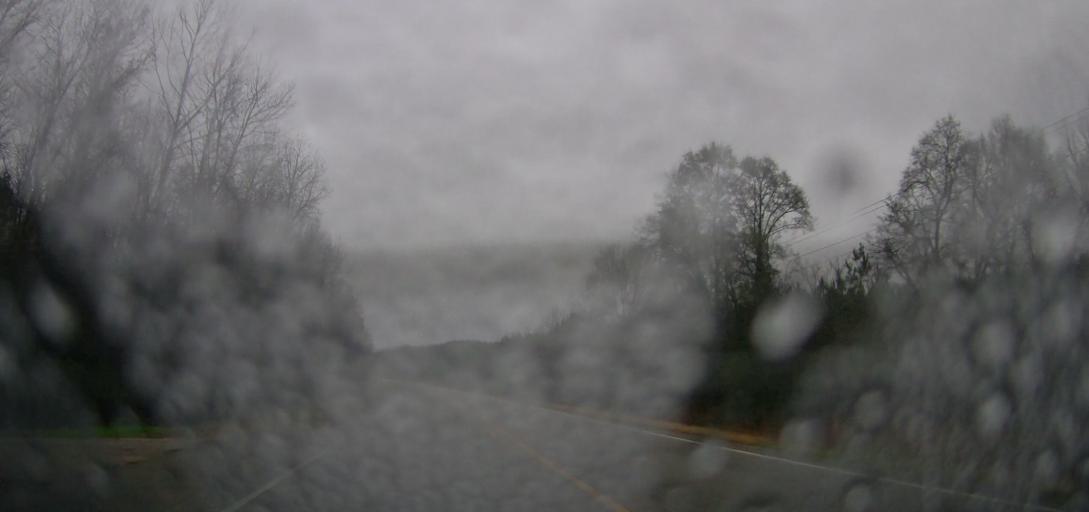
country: US
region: Alabama
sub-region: Autauga County
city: Prattville
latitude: 32.4962
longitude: -86.5803
